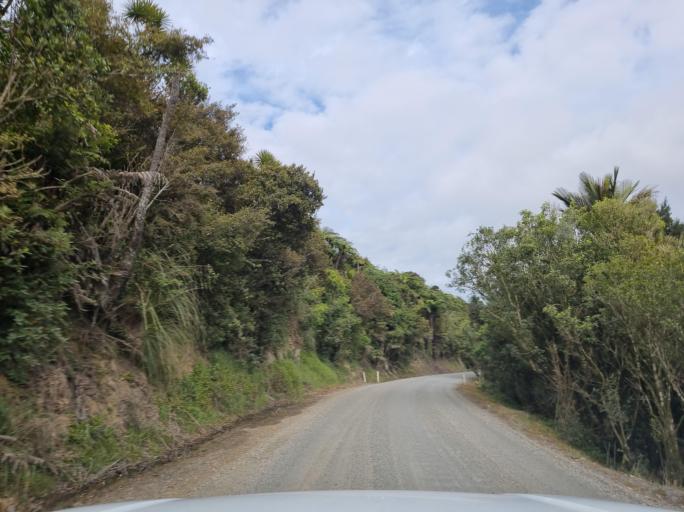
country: NZ
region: Northland
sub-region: Whangarei
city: Ruakaka
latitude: -36.0529
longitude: 174.4020
